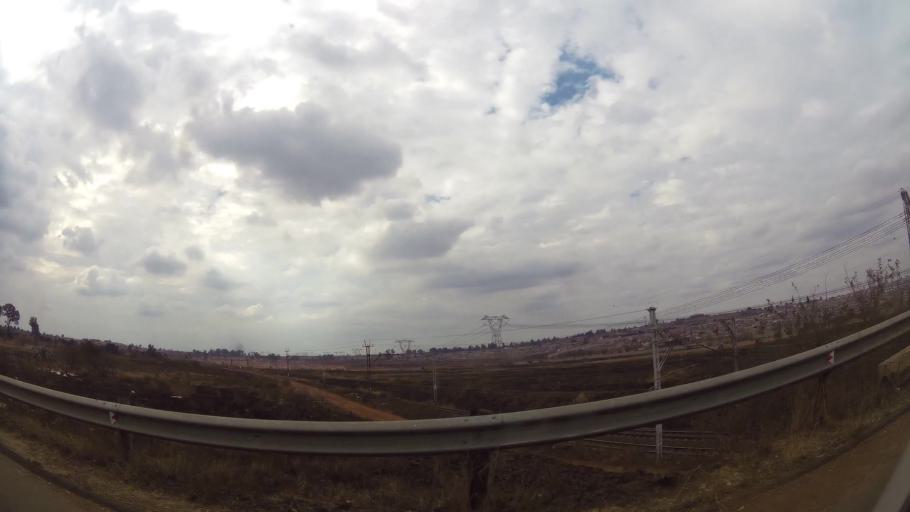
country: ZA
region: Gauteng
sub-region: Ekurhuleni Metropolitan Municipality
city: Germiston
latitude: -26.3782
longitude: 28.1100
